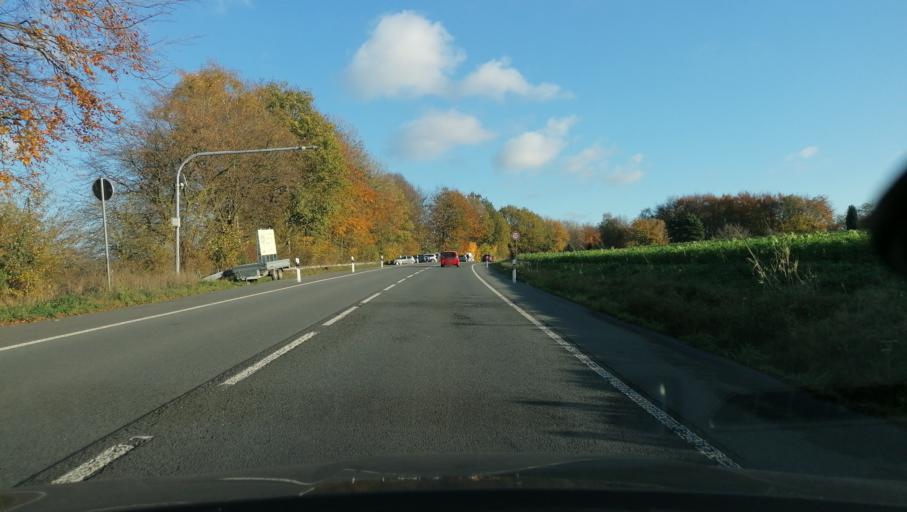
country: DE
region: North Rhine-Westphalia
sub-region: Regierungsbezirk Arnsberg
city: Schwelm
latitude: 51.2762
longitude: 7.3101
